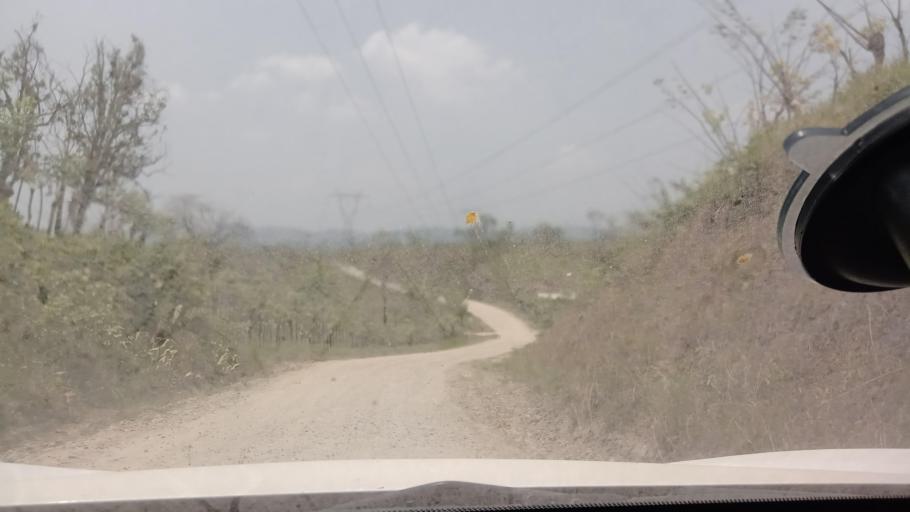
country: MX
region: Chiapas
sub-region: Tecpatan
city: Raudales Malpaso
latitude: 17.4451
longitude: -93.7891
